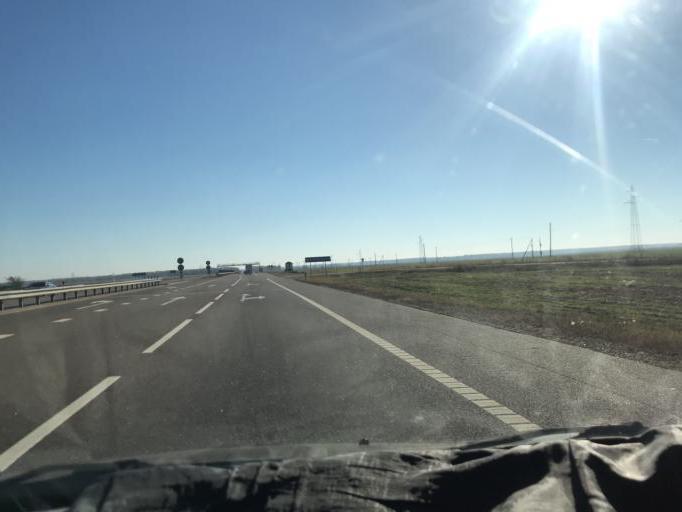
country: BY
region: Mogilev
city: Yalizava
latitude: 53.2350
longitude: 28.9741
